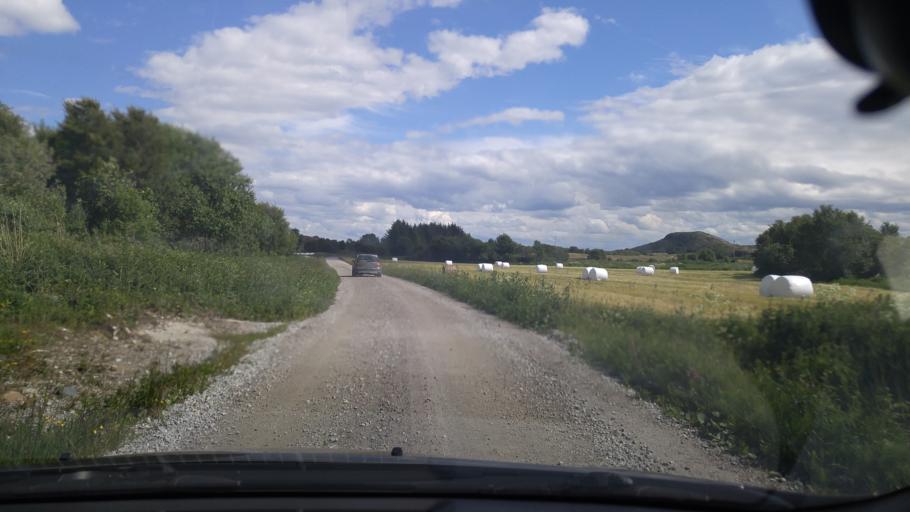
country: NO
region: Nord-Trondelag
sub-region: Vikna
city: Rorvik
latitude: 64.9042
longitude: 11.1206
